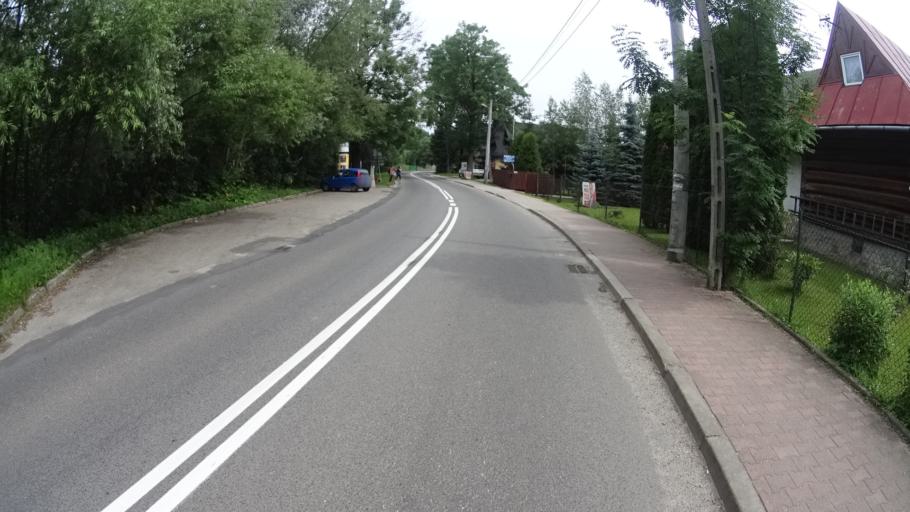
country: PL
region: Lesser Poland Voivodeship
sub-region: Powiat tatrzanski
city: Poronin
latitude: 49.3173
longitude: 19.9803
